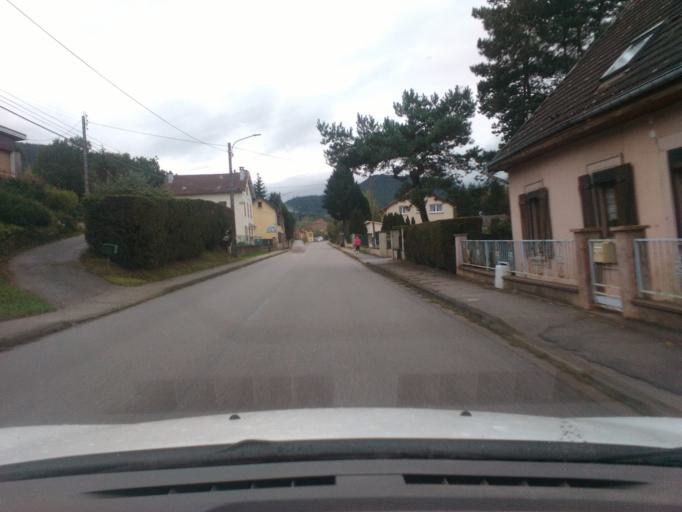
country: FR
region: Lorraine
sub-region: Departement des Vosges
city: Saint-Die-des-Vosges
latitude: 48.2844
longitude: 6.9183
